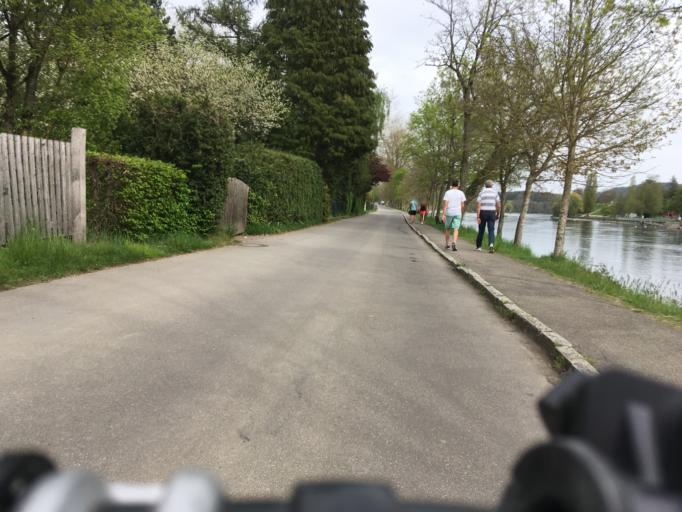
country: CH
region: Thurgau
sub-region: Frauenfeld District
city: Diessenhofen
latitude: 47.6910
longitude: 8.7523
